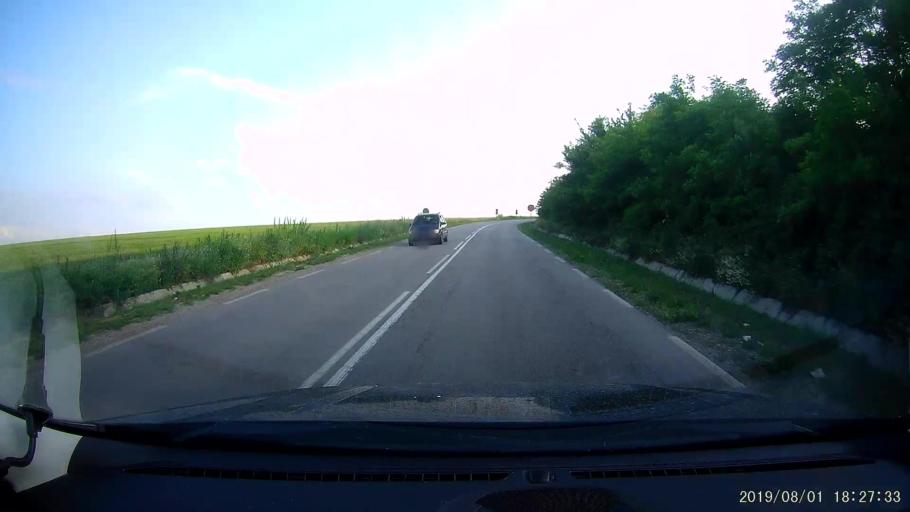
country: BG
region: Shumen
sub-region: Obshtina Venets
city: Venets
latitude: 43.5847
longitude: 26.9811
